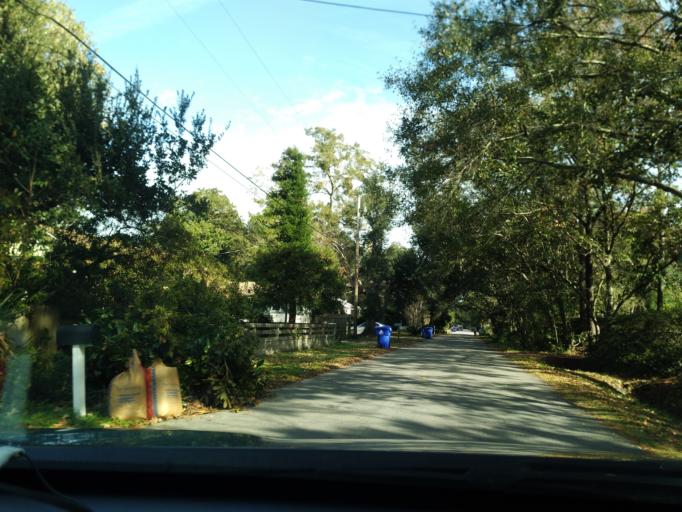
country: US
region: South Carolina
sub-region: Charleston County
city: North Charleston
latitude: 32.8021
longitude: -80.0140
